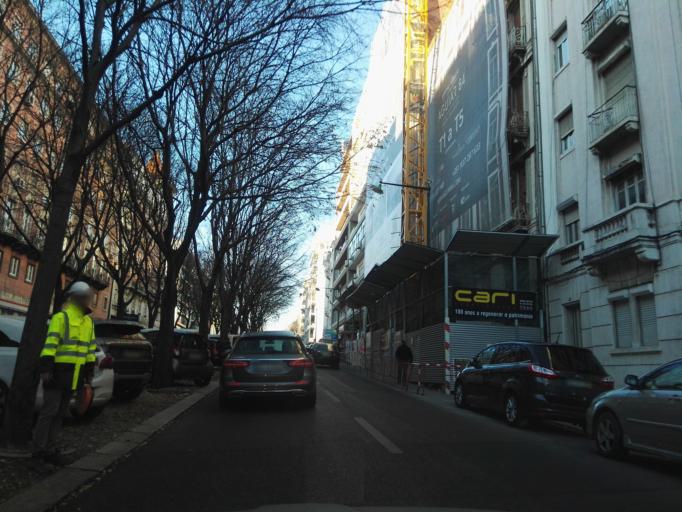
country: PT
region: Lisbon
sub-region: Lisbon
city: Lisbon
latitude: 38.7311
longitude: -9.1513
